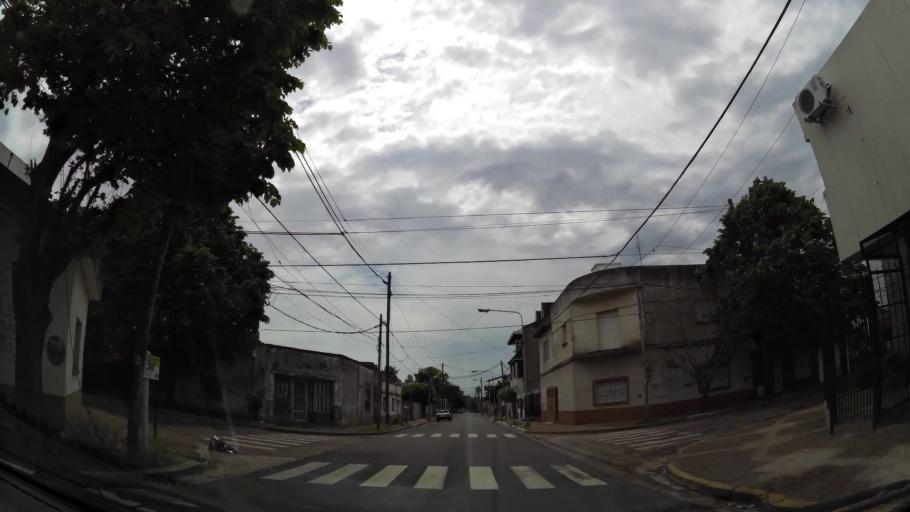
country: AR
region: Buenos Aires
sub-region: Partido de Quilmes
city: Quilmes
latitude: -34.7581
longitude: -58.2051
